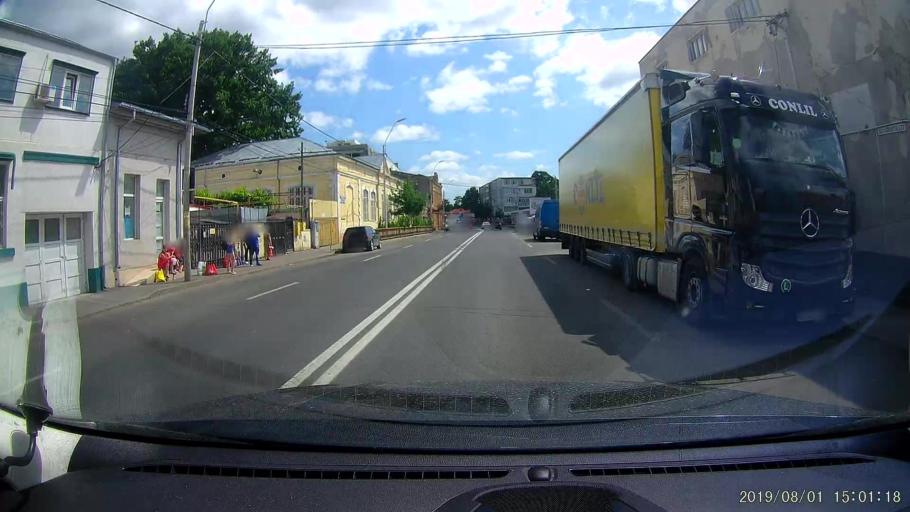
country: RO
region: Braila
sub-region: Municipiul Braila
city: Braila
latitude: 45.2727
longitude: 27.9605
